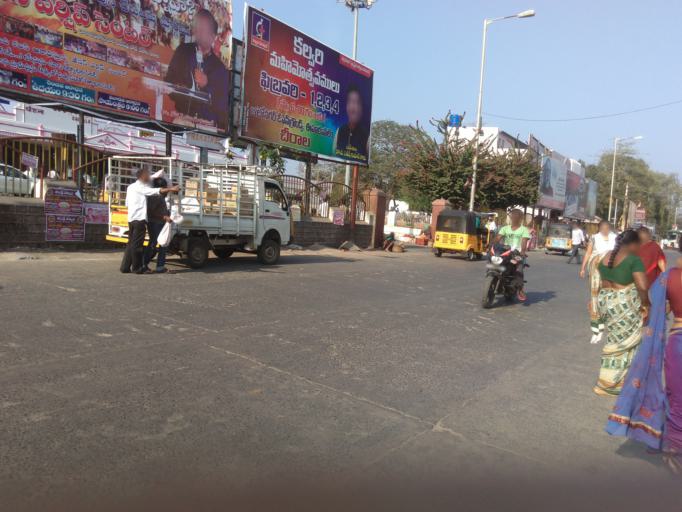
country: IN
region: Andhra Pradesh
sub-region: Prakasam
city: Chirala
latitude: 15.8305
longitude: 80.3544
